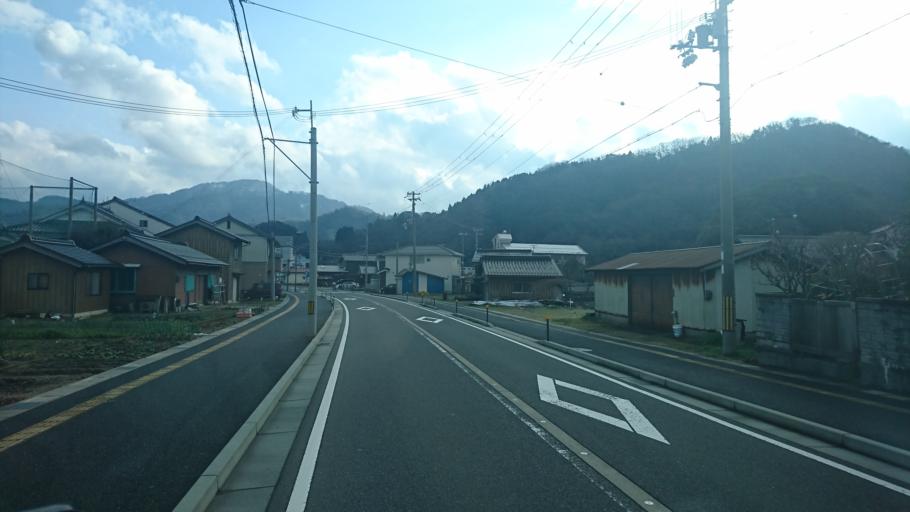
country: JP
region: Tottori
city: Tottori
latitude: 35.6260
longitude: 134.4453
